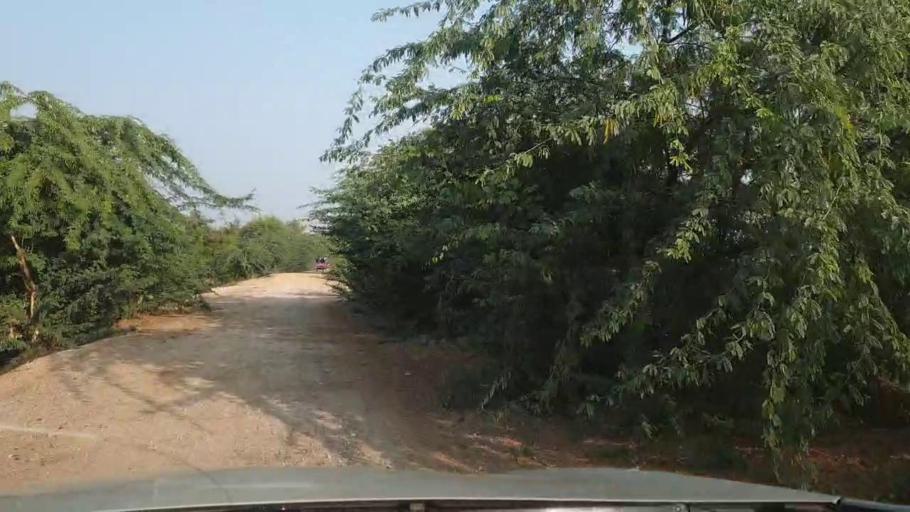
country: PK
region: Sindh
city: Sehwan
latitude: 26.3462
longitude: 67.7236
